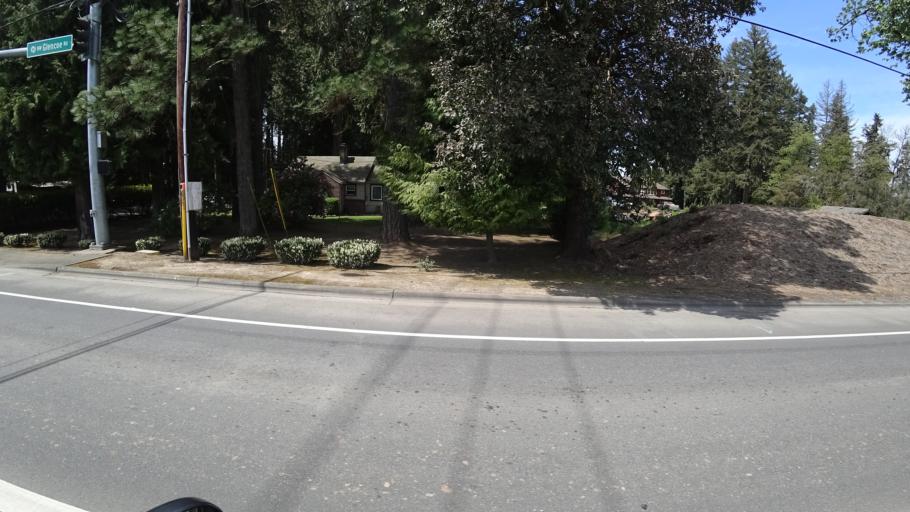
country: US
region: Oregon
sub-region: Washington County
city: Hillsboro
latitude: 45.5499
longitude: -122.9955
